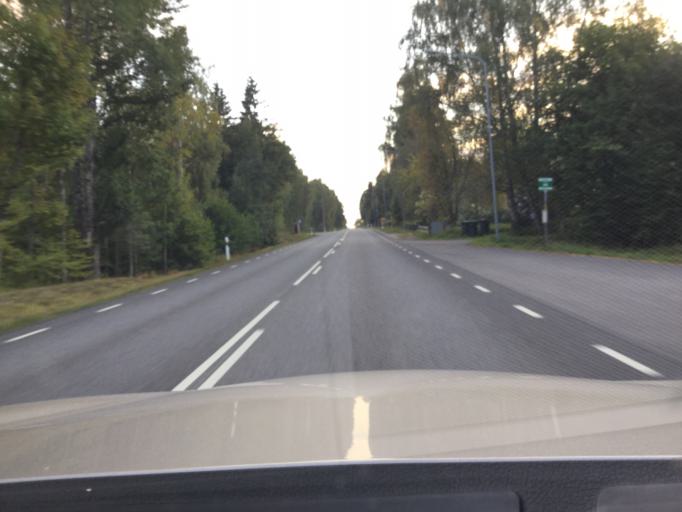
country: SE
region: Kronoberg
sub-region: Almhults Kommun
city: AElmhult
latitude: 56.6229
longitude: 14.1983
